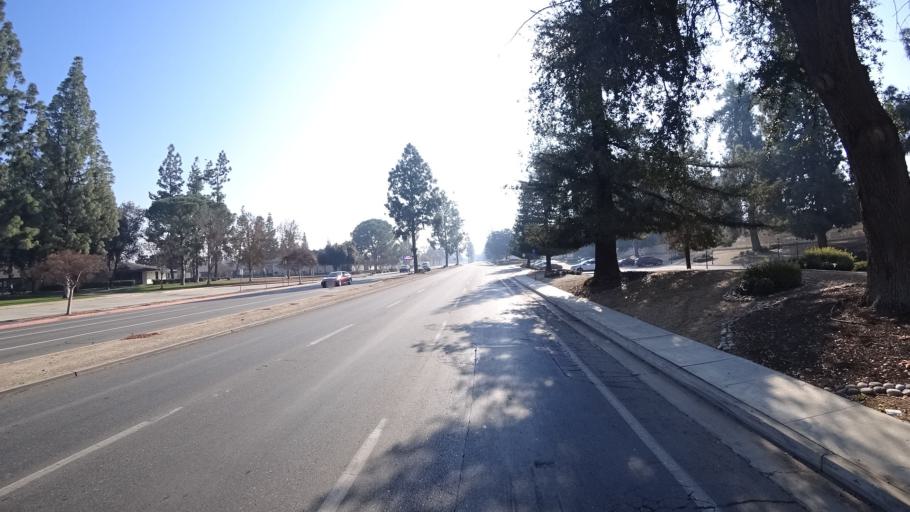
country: US
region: California
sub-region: Kern County
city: Bakersfield
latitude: 35.3440
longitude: -119.0612
